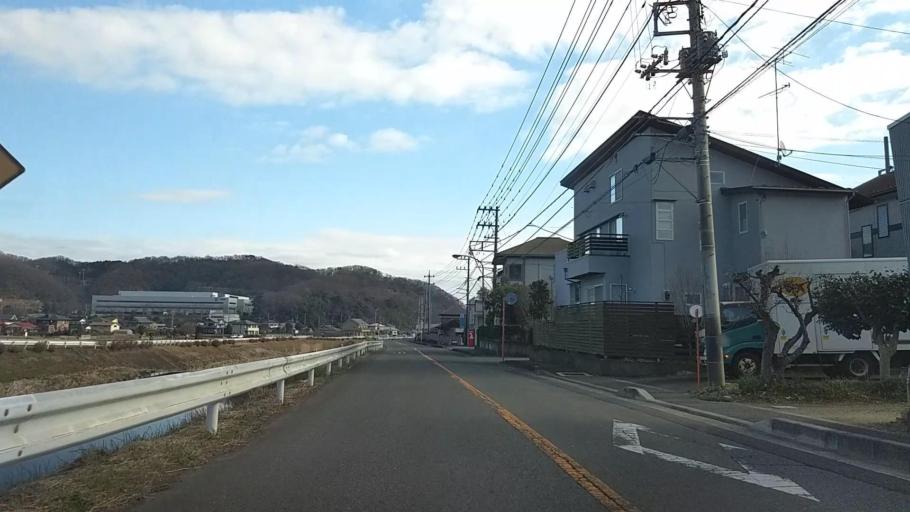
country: JP
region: Kanagawa
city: Isehara
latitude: 35.4352
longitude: 139.3085
